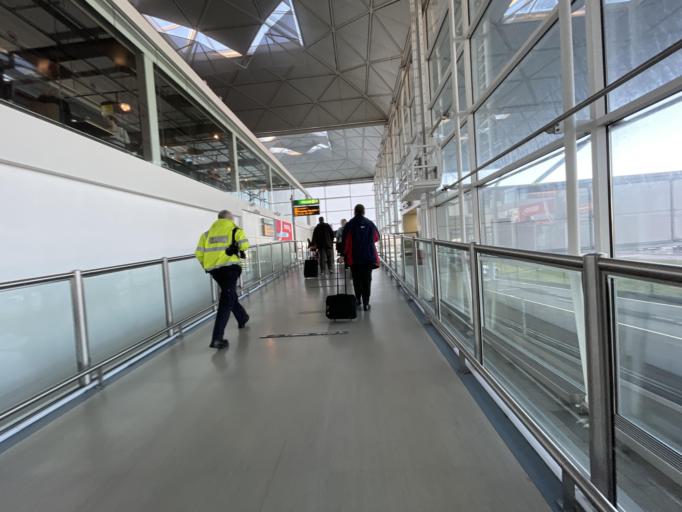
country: GB
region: England
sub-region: Essex
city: Takeley
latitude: 51.8898
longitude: 0.2600
